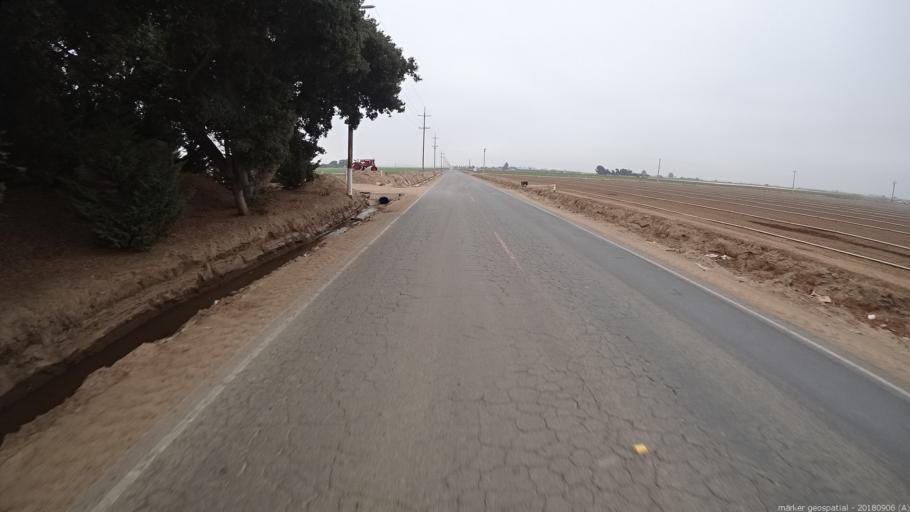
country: US
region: California
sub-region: Monterey County
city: Chualar
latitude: 36.6374
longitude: -121.5614
